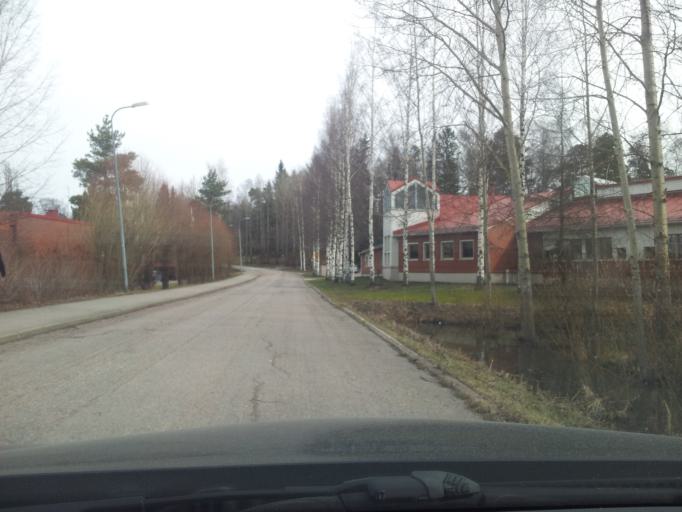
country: FI
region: Uusimaa
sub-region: Helsinki
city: Koukkuniemi
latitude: 60.1801
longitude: 24.7872
